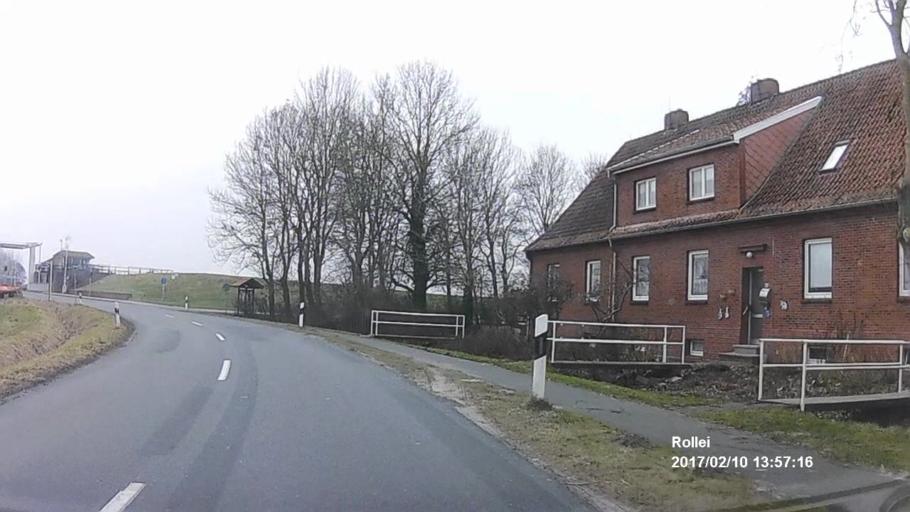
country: DE
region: Lower Saxony
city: Norddeich
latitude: 53.5435
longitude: 7.1431
